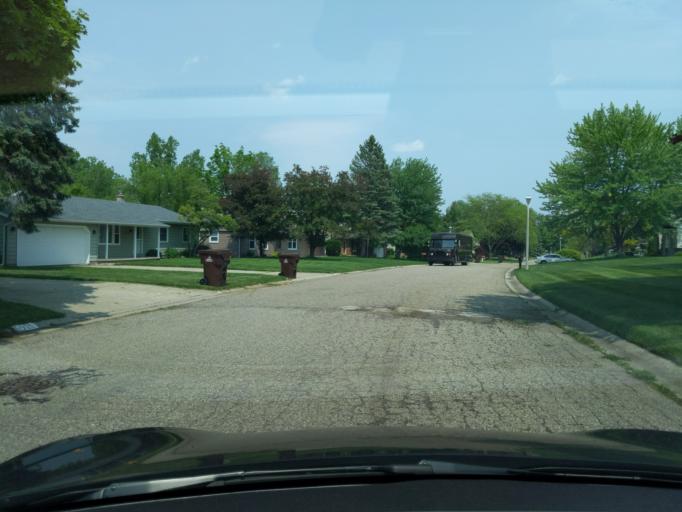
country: US
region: Michigan
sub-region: Eaton County
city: Waverly
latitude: 42.7577
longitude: -84.6506
